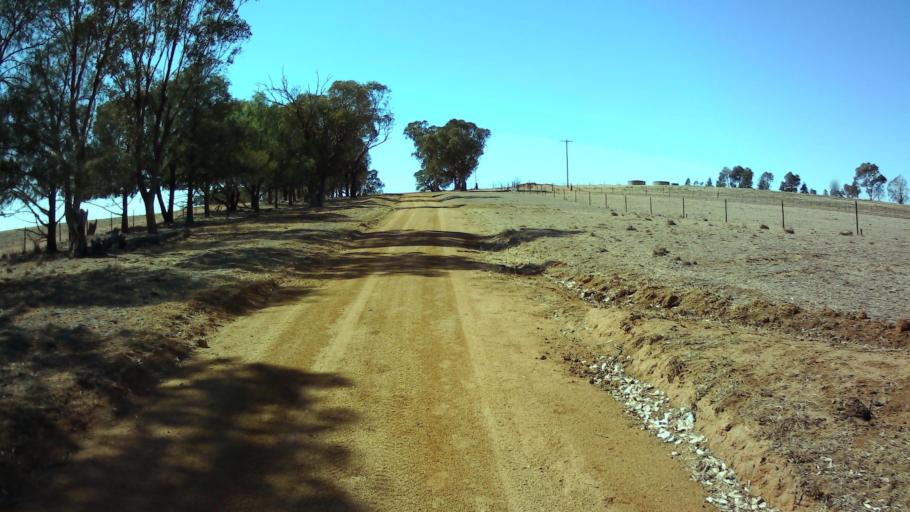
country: AU
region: New South Wales
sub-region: Cowra
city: Cowra
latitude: -33.9735
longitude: 148.4620
